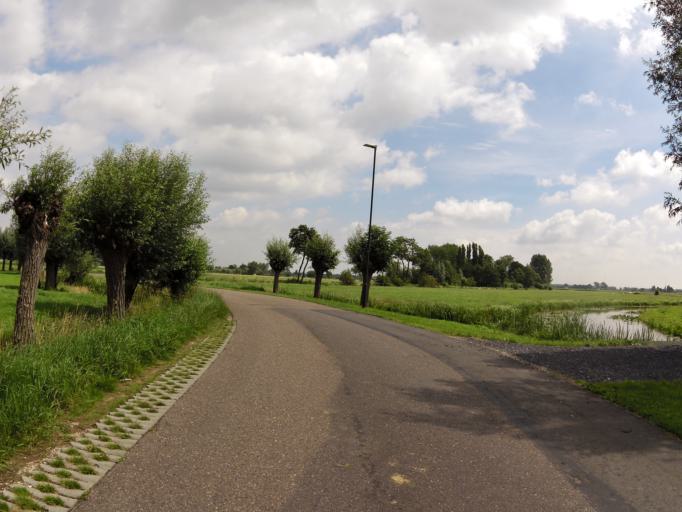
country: NL
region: South Holland
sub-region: Gemeente Gorinchem
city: Gorinchem
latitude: 51.8852
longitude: 4.9635
